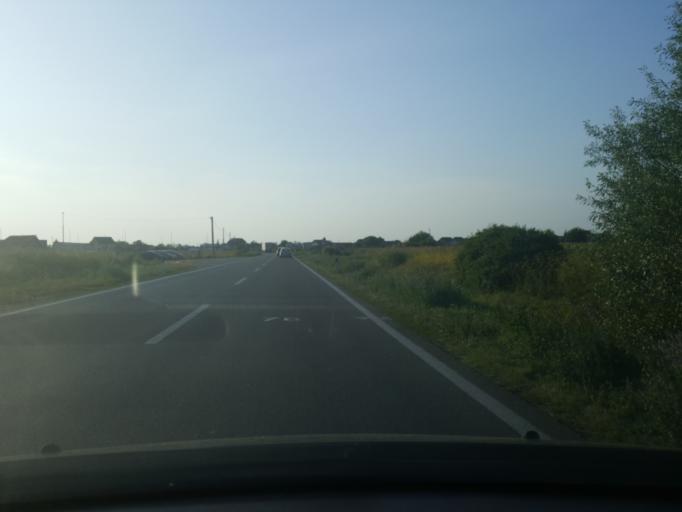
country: RS
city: Majur
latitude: 44.7704
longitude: 19.6264
